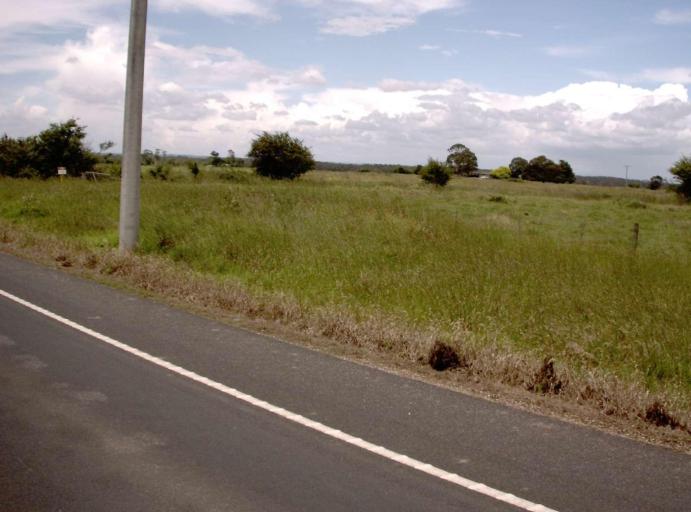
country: AU
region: Victoria
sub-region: Wellington
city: Sale
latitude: -38.0407
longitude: 147.0191
